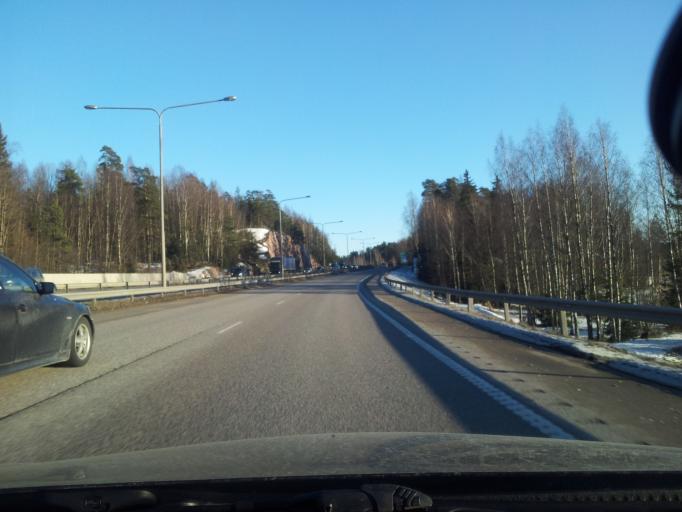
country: FI
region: Uusimaa
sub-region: Helsinki
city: Espoo
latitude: 60.2261
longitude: 24.6075
